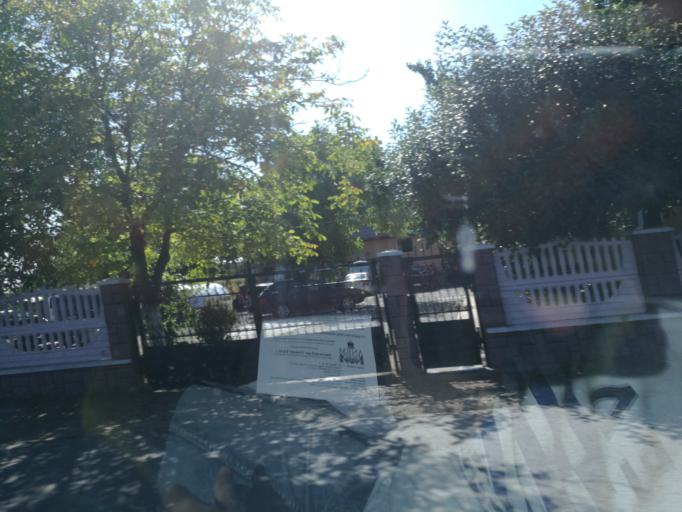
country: RO
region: Suceava
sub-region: Municipiul Suceava
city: Radauti
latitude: 47.8308
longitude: 25.9345
